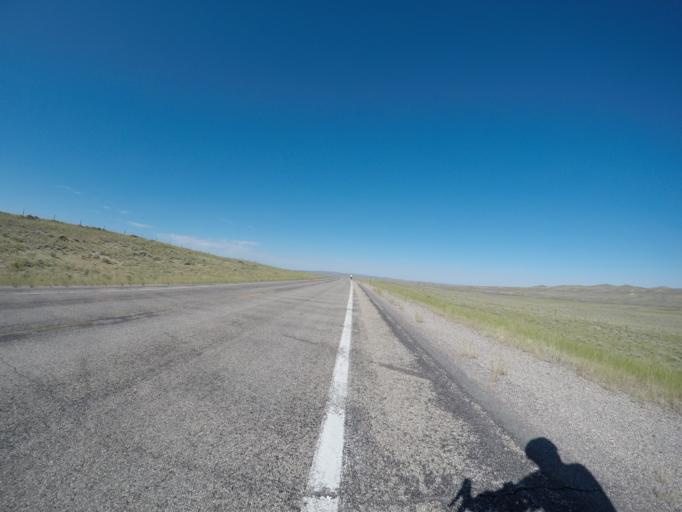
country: US
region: Wyoming
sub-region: Carbon County
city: Saratoga
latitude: 41.8852
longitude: -106.4759
